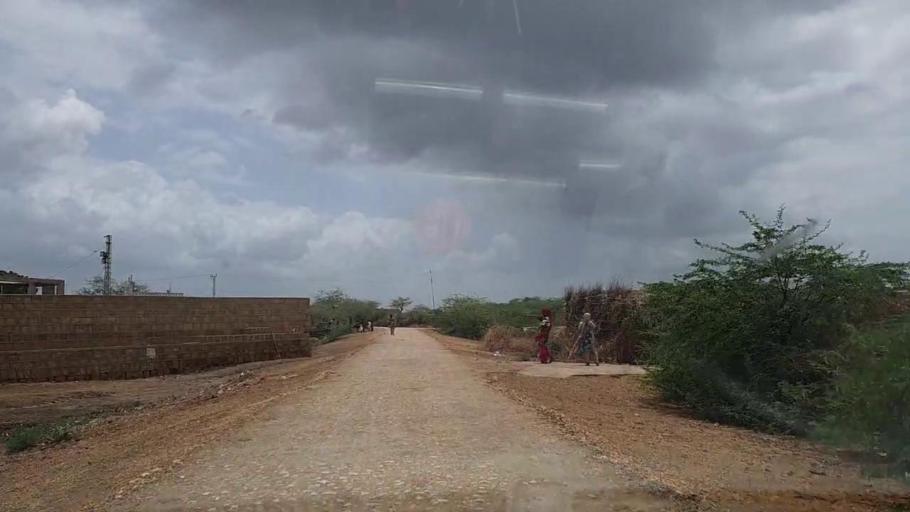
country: PK
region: Sindh
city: Thatta
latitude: 24.6213
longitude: 68.0266
